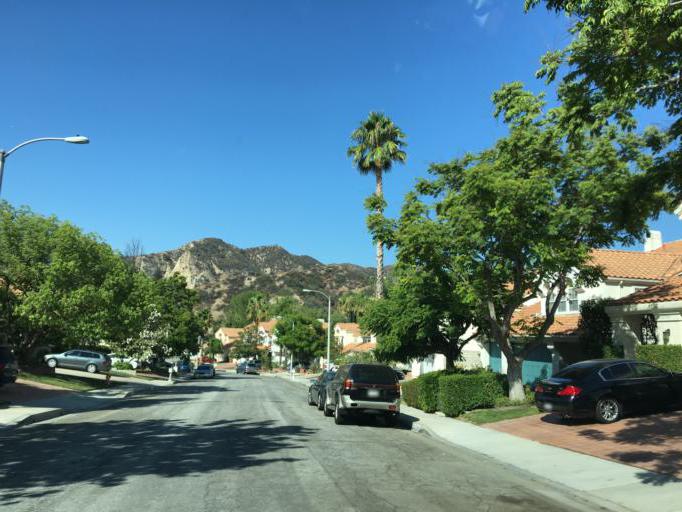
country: US
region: California
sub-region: Los Angeles County
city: Santa Clarita
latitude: 34.3854
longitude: -118.5832
